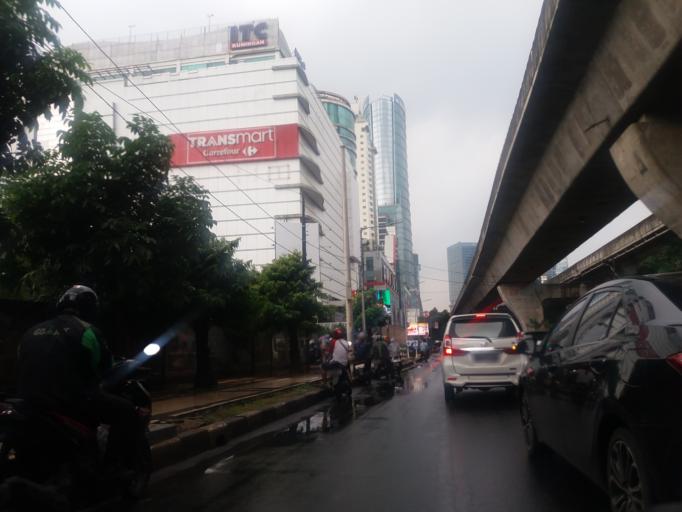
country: ID
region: Jakarta Raya
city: Jakarta
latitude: -6.2237
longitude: 106.8249
